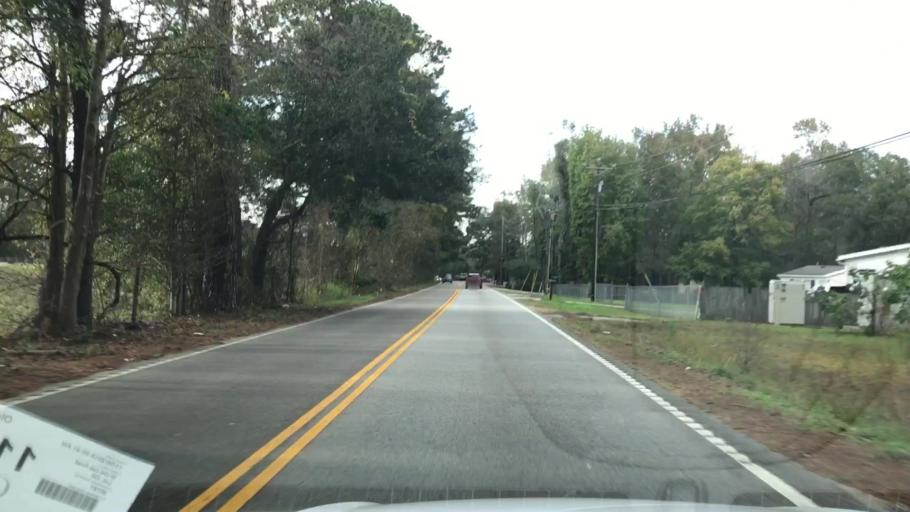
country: US
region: South Carolina
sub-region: Berkeley County
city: Ladson
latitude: 33.0043
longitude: -80.1003
